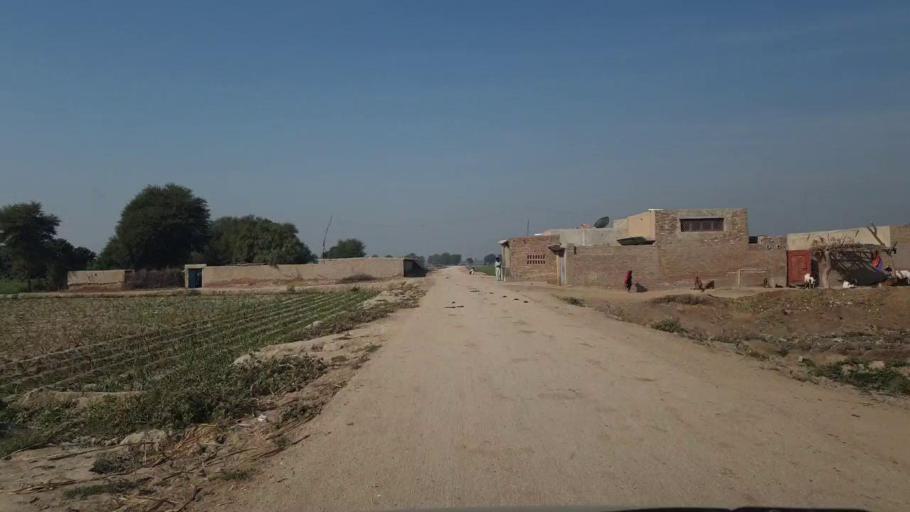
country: PK
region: Sindh
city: Tando Allahyar
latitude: 25.4047
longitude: 68.7376
